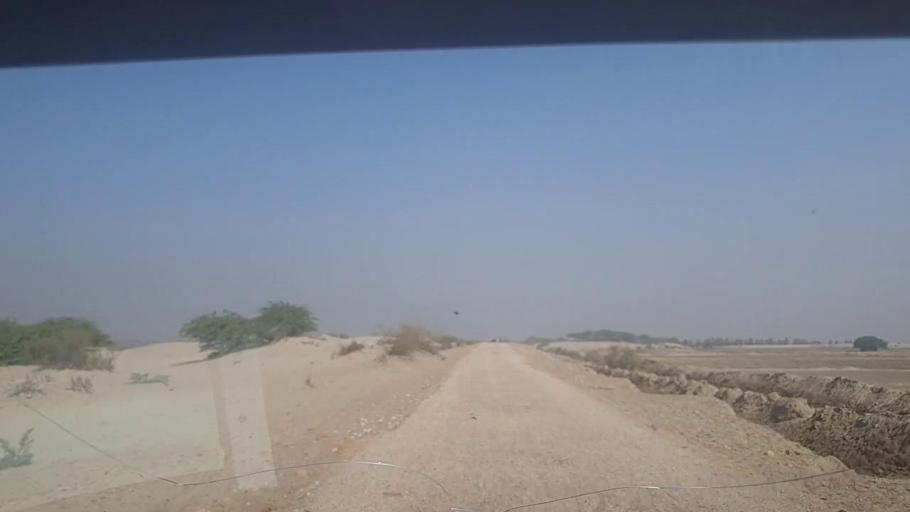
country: PK
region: Sindh
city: Khairpur
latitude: 27.4493
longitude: 68.7200
